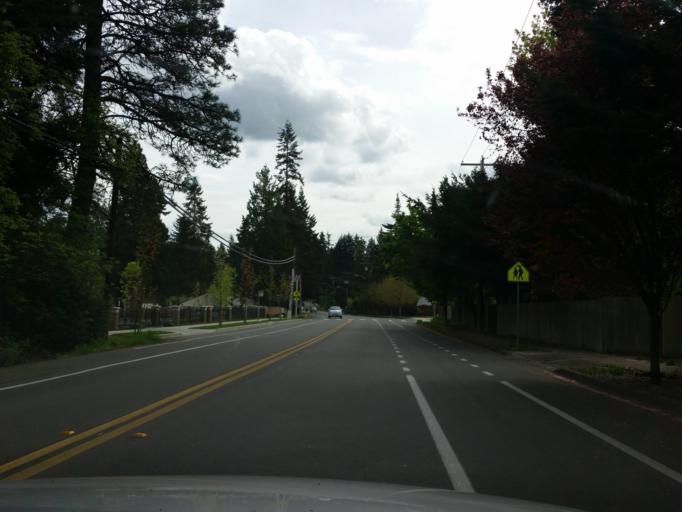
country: US
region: Washington
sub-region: King County
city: Kingsgate
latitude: 47.6904
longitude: -122.1650
